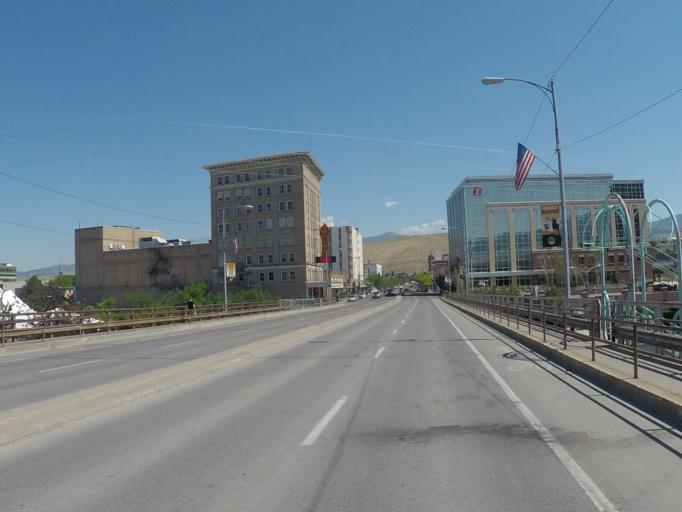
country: US
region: Montana
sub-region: Missoula County
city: Missoula
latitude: 46.8685
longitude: -113.9963
